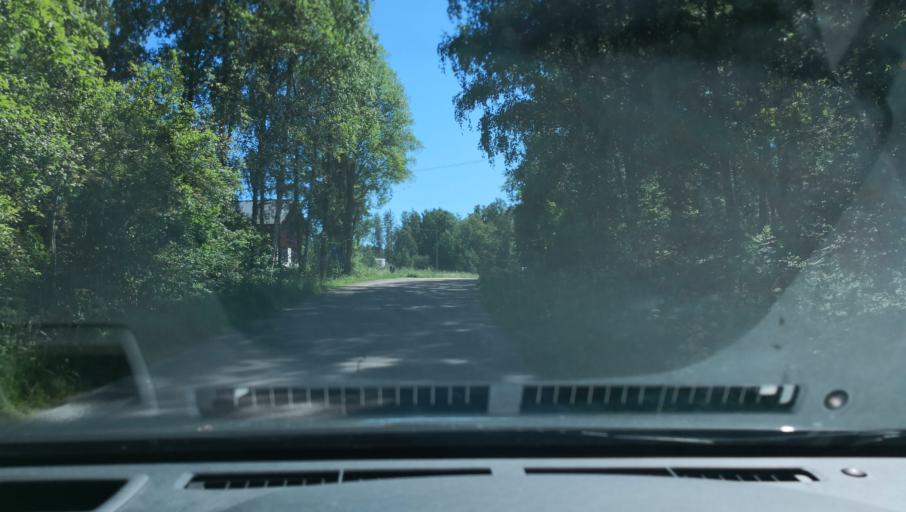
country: SE
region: Vaestmanland
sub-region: Arboga Kommun
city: Tyringe
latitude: 59.3847
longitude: 15.9454
